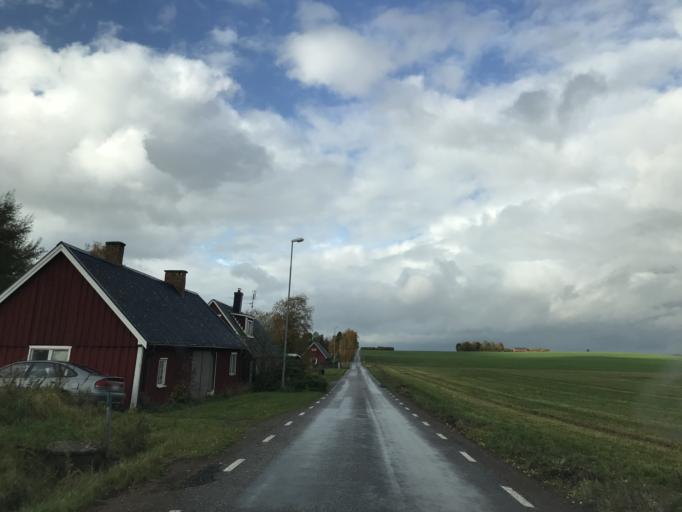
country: SE
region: Skane
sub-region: Svalovs Kommun
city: Svaloev
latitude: 55.9024
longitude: 13.1843
